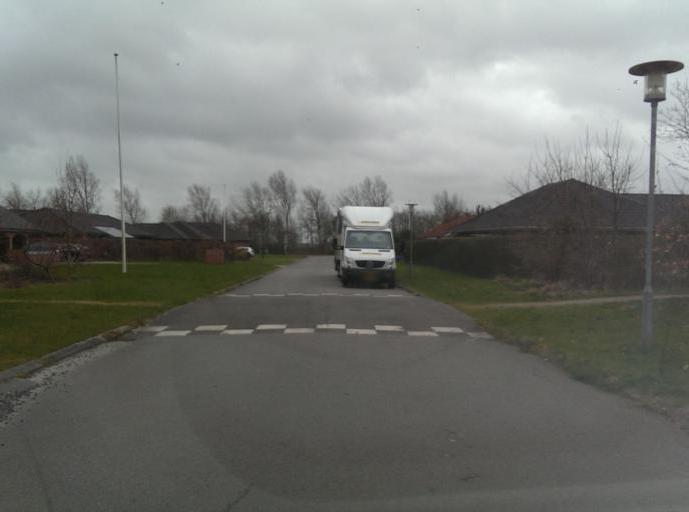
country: DK
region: South Denmark
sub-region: Esbjerg Kommune
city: Tjaereborg
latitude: 55.4581
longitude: 8.5984
